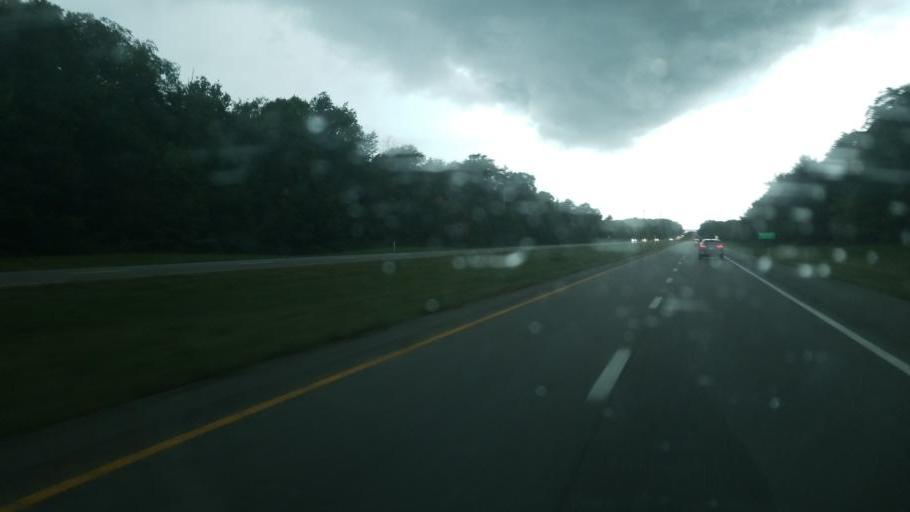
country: US
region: Ohio
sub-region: Geauga County
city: Bainbridge
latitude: 41.3825
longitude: -81.2960
